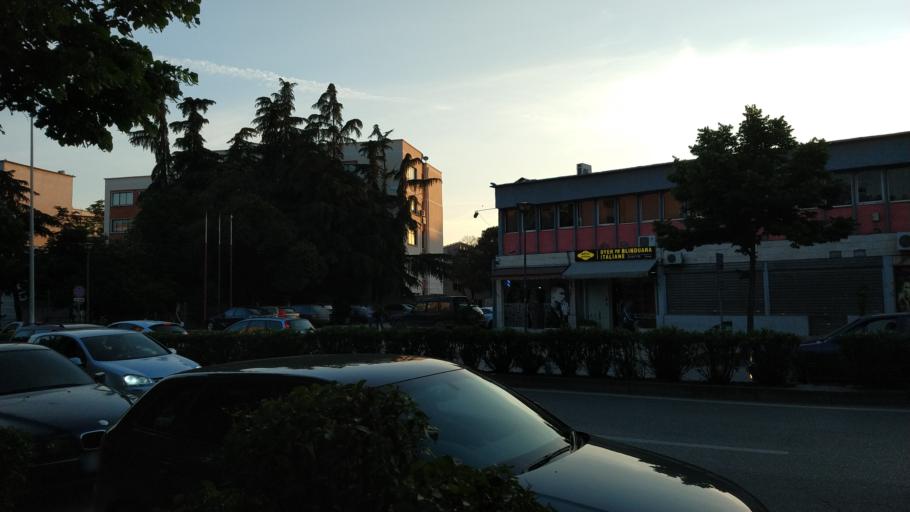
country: AL
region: Tirane
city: Tirana
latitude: 41.3293
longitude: 19.8029
